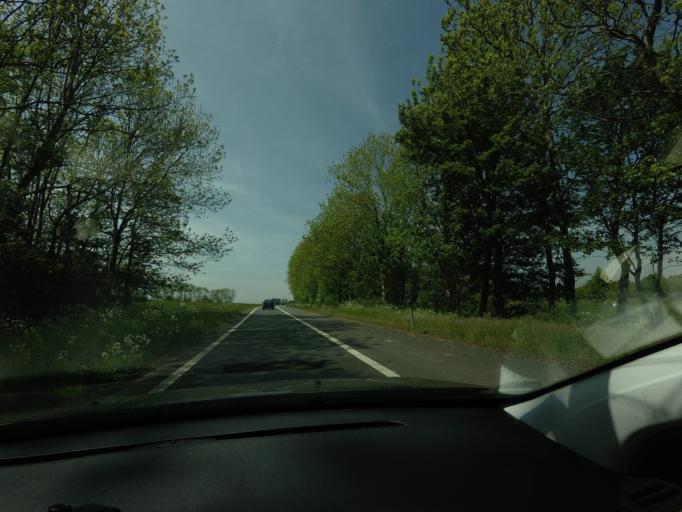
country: NL
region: Friesland
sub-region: Sudwest Fryslan
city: Bolsward
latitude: 53.0482
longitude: 5.5709
